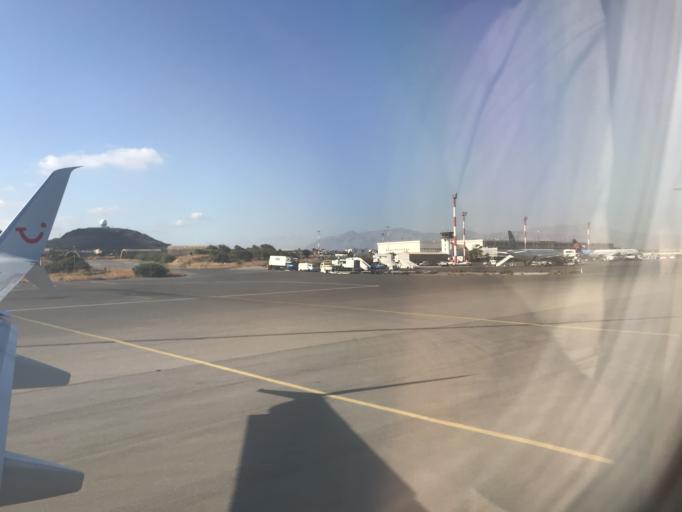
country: GR
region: Crete
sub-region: Nomos Irakleiou
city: Nea Alikarnassos
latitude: 35.3389
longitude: 25.1788
